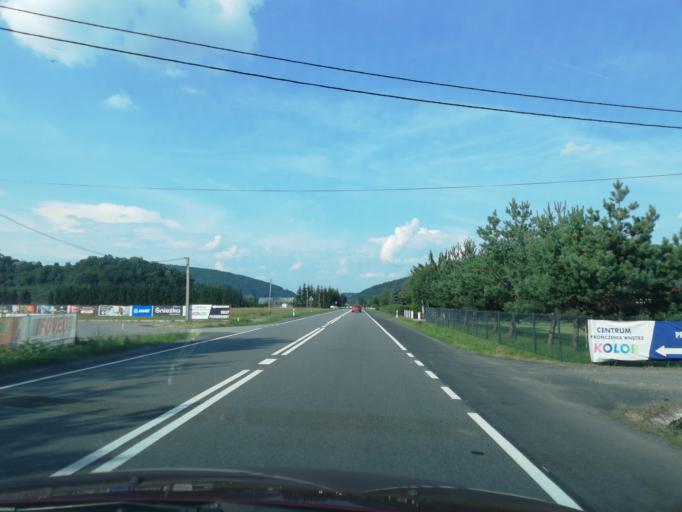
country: PL
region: Lesser Poland Voivodeship
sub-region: Powiat nowosadecki
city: Lososina Dolna
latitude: 49.7501
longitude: 20.6324
